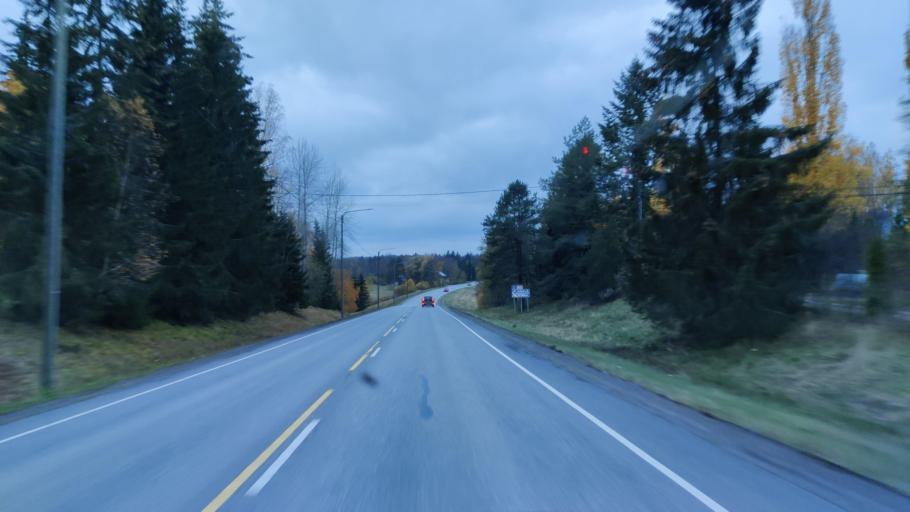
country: FI
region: Uusimaa
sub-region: Helsinki
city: Saukkola
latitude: 60.3720
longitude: 24.1144
